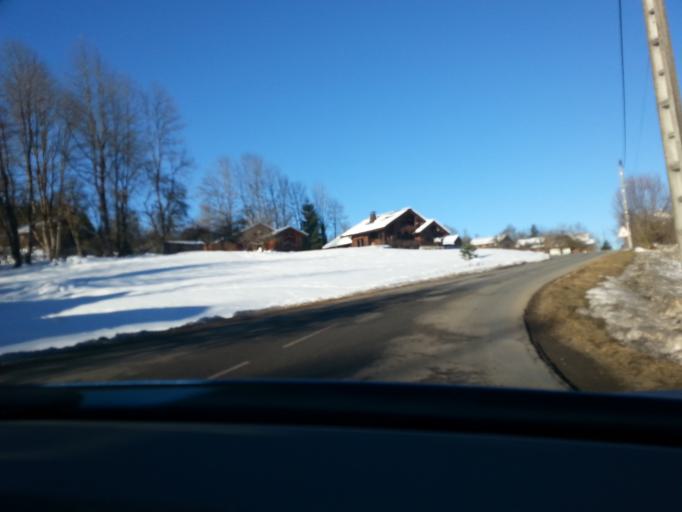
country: FR
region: Rhone-Alpes
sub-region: Departement de la Haute-Savoie
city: Samoens
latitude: 46.0745
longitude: 6.7064
